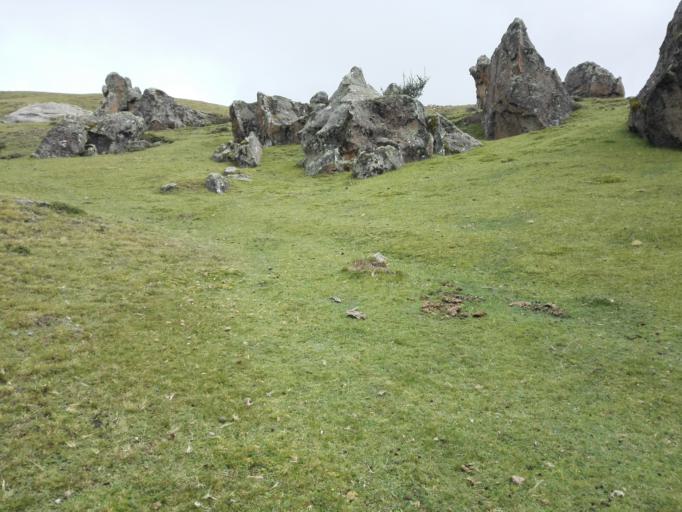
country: PE
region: Ayacucho
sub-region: Provincia de Huamanga
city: Vinchos
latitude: -13.3174
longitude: -74.4514
